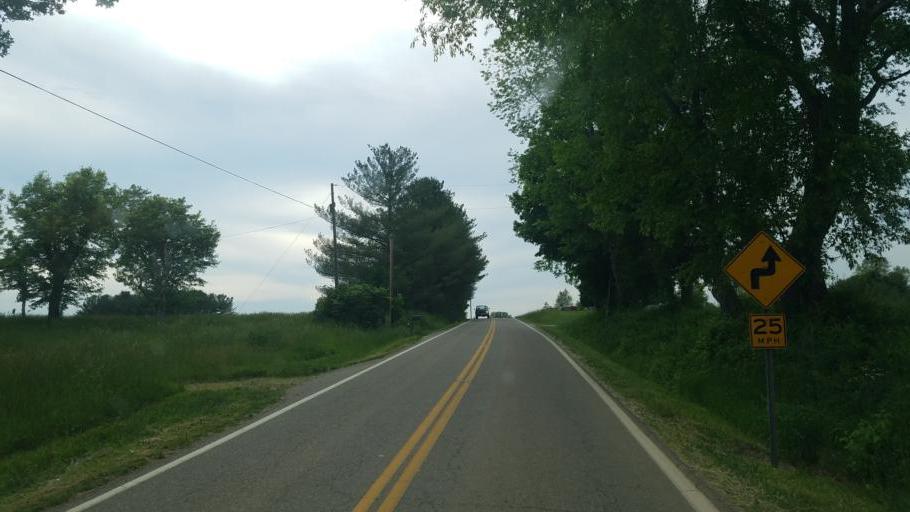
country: US
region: Ohio
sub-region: Athens County
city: Athens
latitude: 39.1619
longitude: -82.2349
